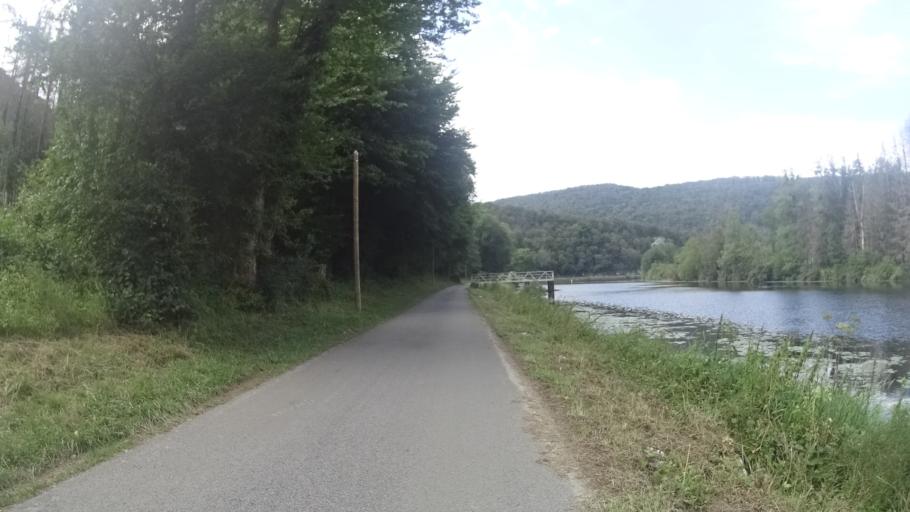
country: FR
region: Franche-Comte
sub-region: Departement du Doubs
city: Clerval
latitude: 47.3669
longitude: 6.4336
